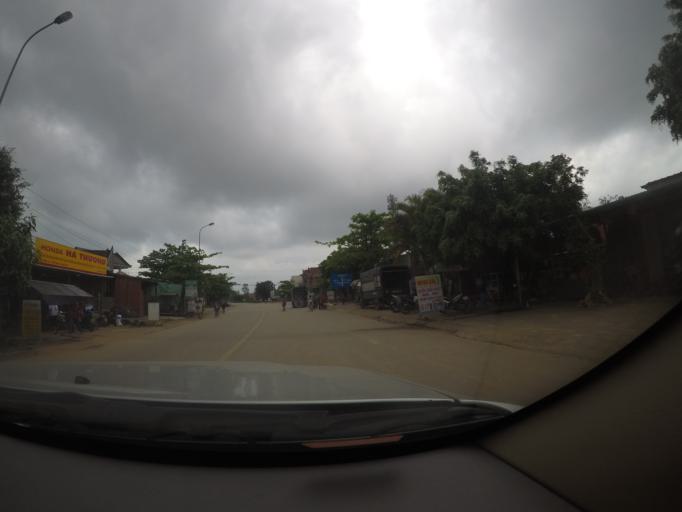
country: VN
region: Quang Tri
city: Ho Xa
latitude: 17.0223
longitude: 106.9016
